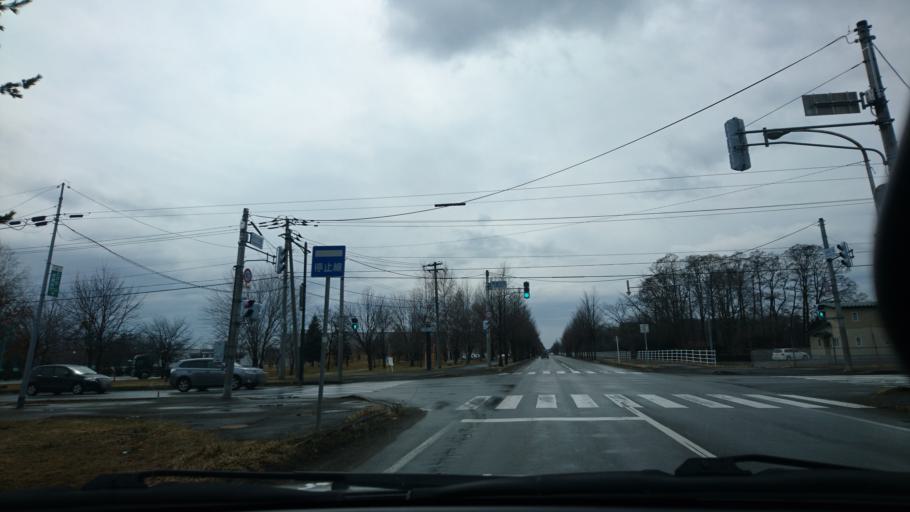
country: JP
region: Hokkaido
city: Otofuke
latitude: 42.9916
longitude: 143.1893
